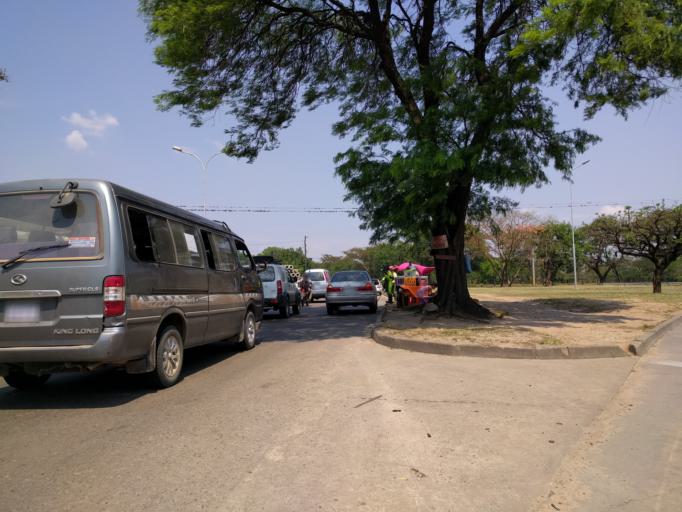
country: BO
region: Santa Cruz
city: Santa Cruz de la Sierra
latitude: -17.8103
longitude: -63.1611
